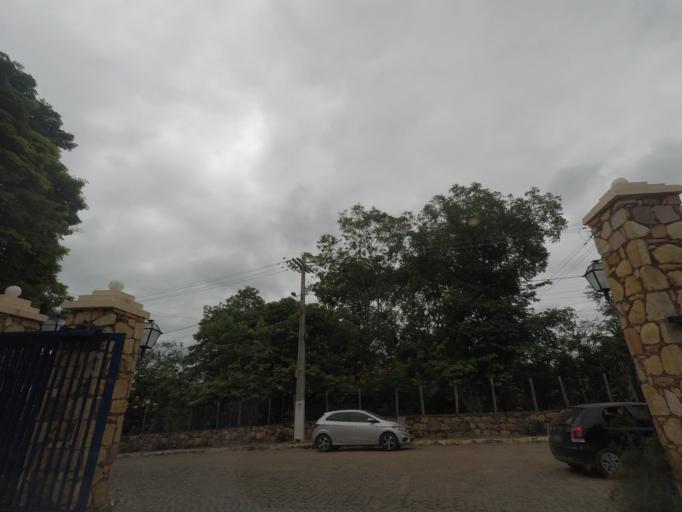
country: BR
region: Bahia
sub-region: Andarai
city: Vera Cruz
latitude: -12.5654
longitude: -41.3949
